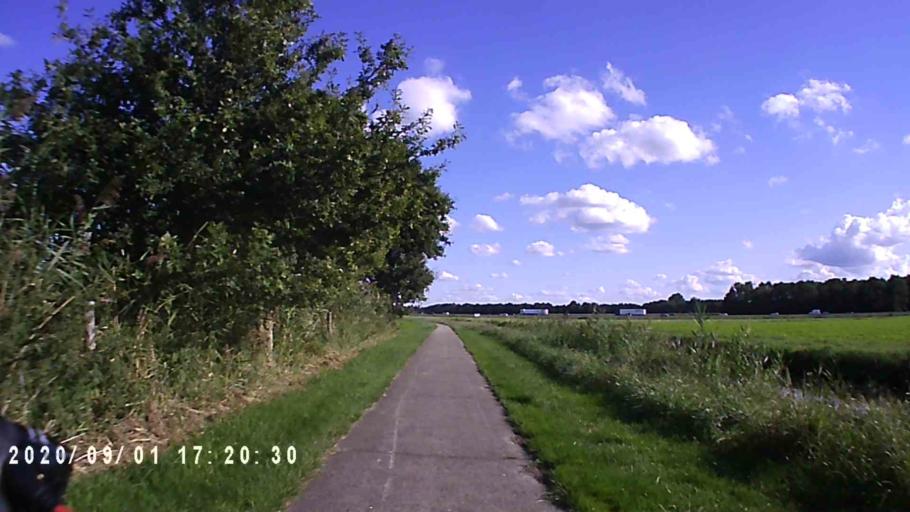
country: NL
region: Groningen
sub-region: Gemeente Haren
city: Haren
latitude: 53.2031
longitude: 6.6663
